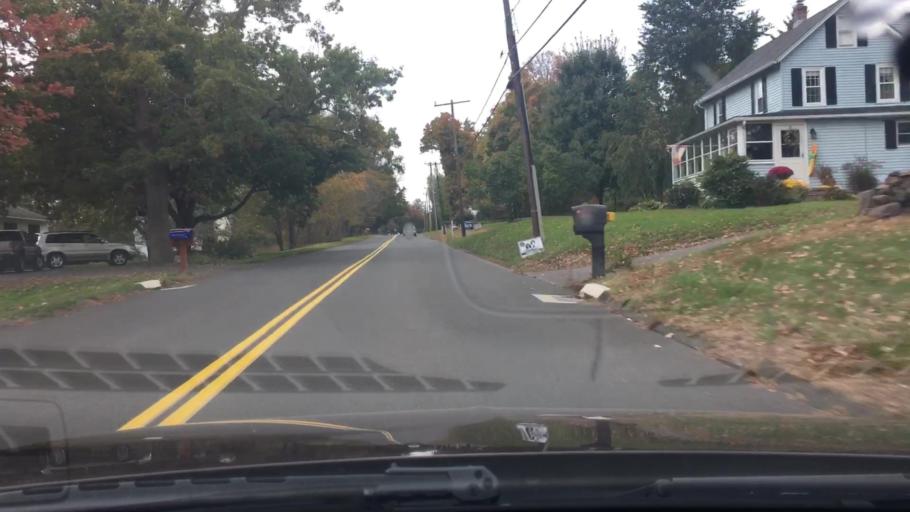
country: US
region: Connecticut
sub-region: Tolland County
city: Ellington
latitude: 41.9228
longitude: -72.4761
